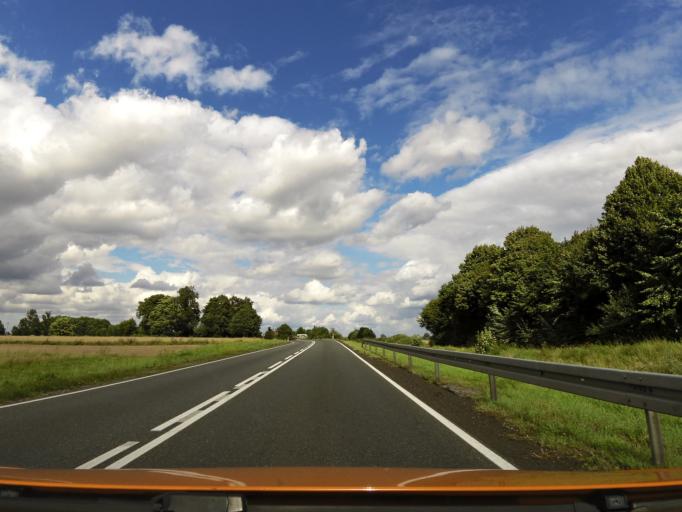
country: PL
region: West Pomeranian Voivodeship
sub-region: Powiat goleniowski
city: Nowogard
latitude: 53.7139
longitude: 15.1847
